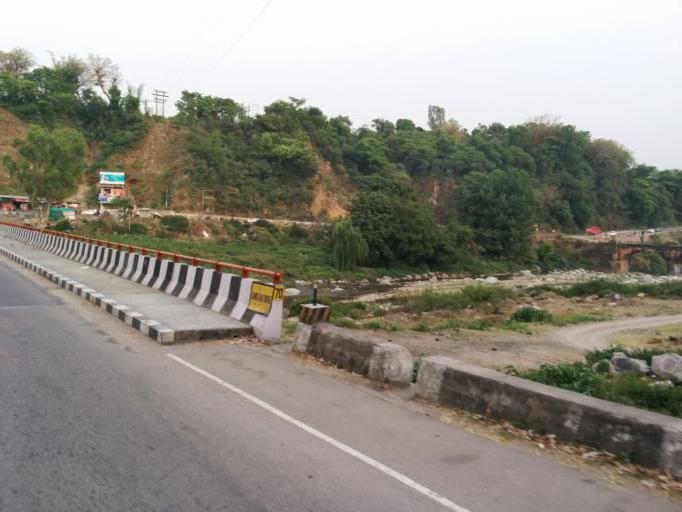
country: IN
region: Himachal Pradesh
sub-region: Kangra
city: Yol
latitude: 32.1870
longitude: 76.2174
